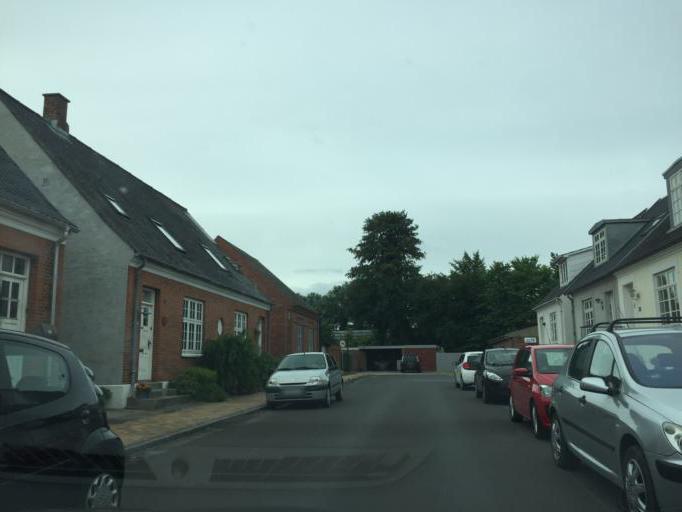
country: DK
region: South Denmark
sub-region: Middelfart Kommune
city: Middelfart
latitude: 55.5015
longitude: 9.7423
